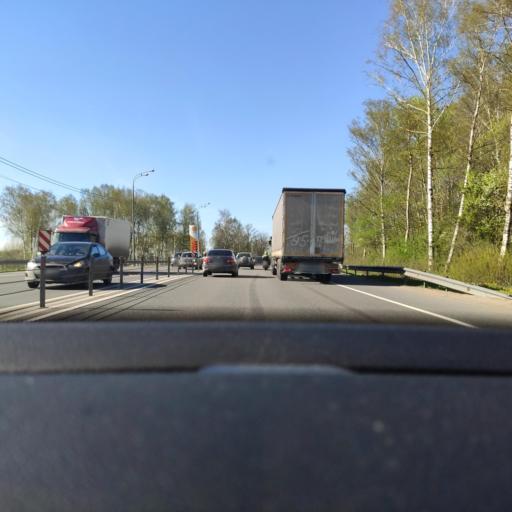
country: RU
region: Moskovskaya
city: Dedenevo
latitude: 56.2625
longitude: 37.5036
